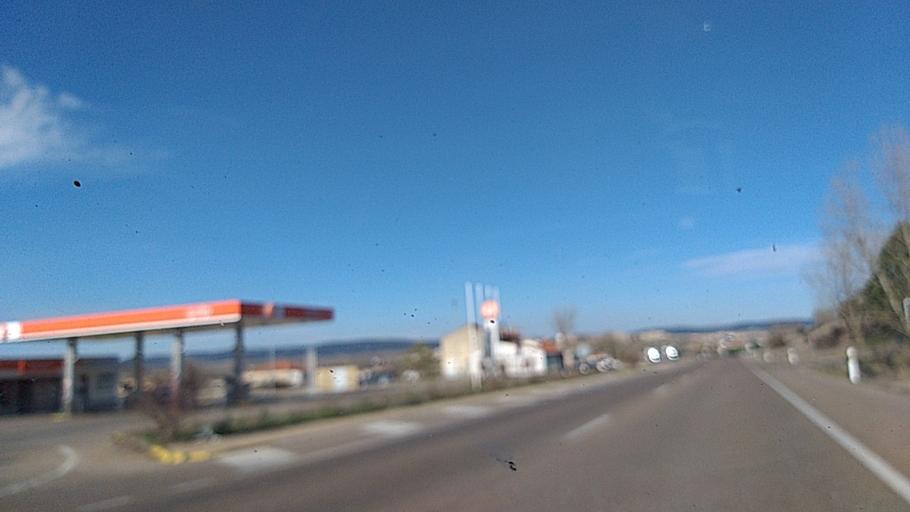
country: ES
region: Castille and Leon
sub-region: Provincia de Salamanca
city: Ciudad Rodrigo
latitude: 40.5810
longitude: -6.5559
